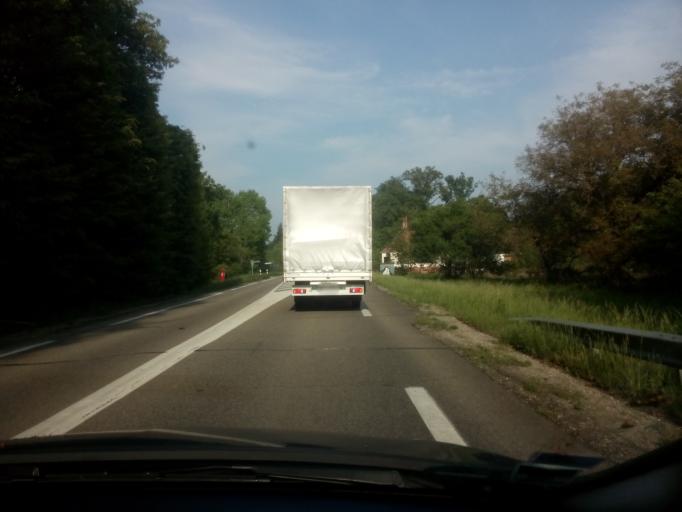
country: FR
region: Alsace
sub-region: Departement du Bas-Rhin
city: Kaltenhouse
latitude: 48.8333
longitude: 7.8553
